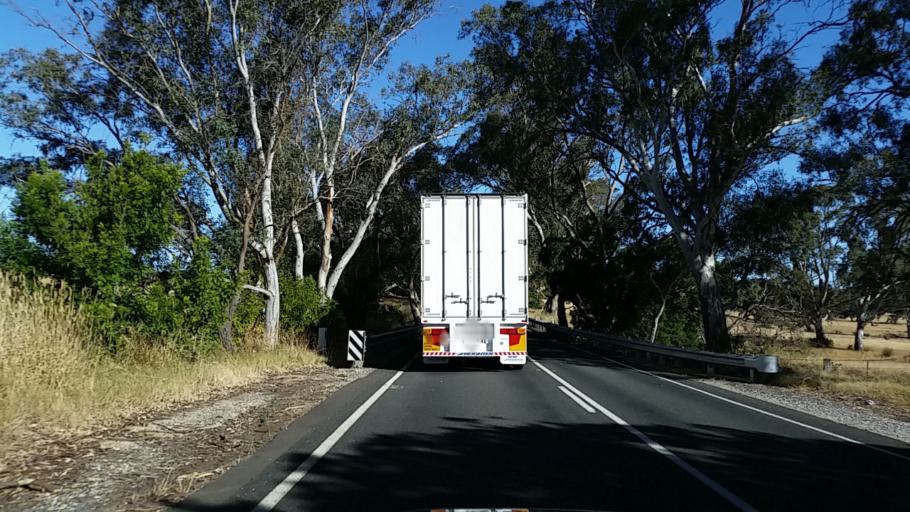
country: AU
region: South Australia
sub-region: Adelaide Hills
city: Birdwood
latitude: -34.7664
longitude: 139.0190
